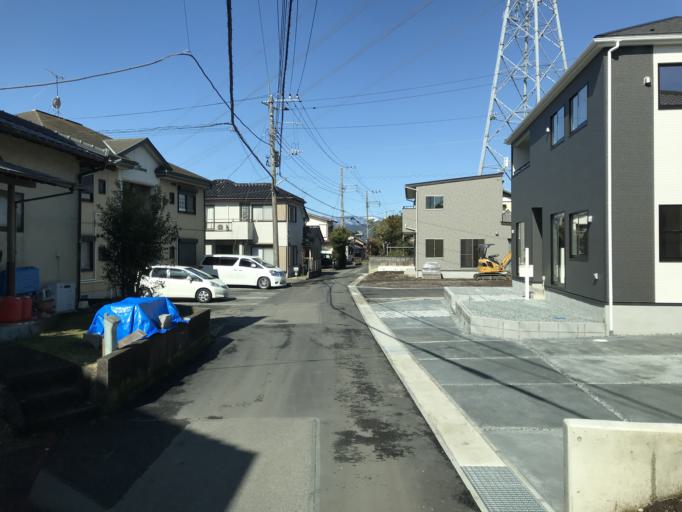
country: JP
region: Shizuoka
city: Fujinomiya
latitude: 35.2575
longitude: 138.6307
